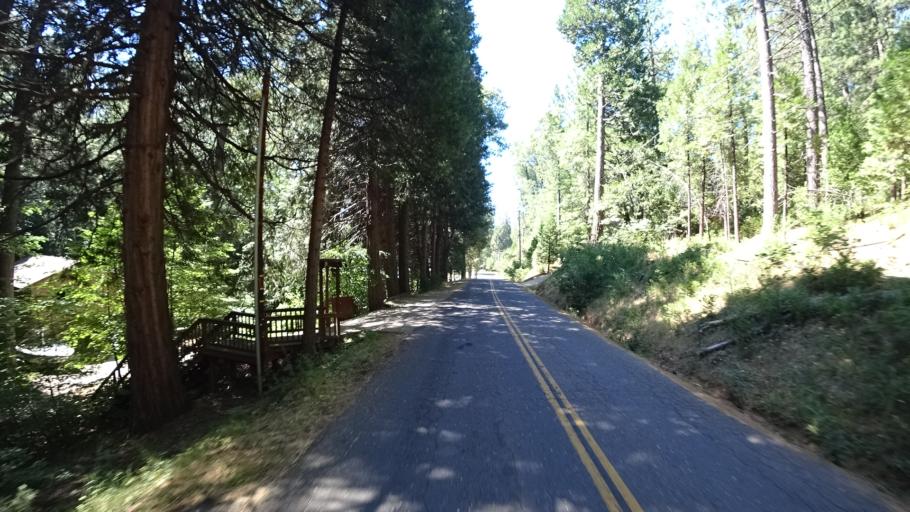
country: US
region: California
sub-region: Calaveras County
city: Arnold
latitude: 38.2389
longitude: -120.3773
